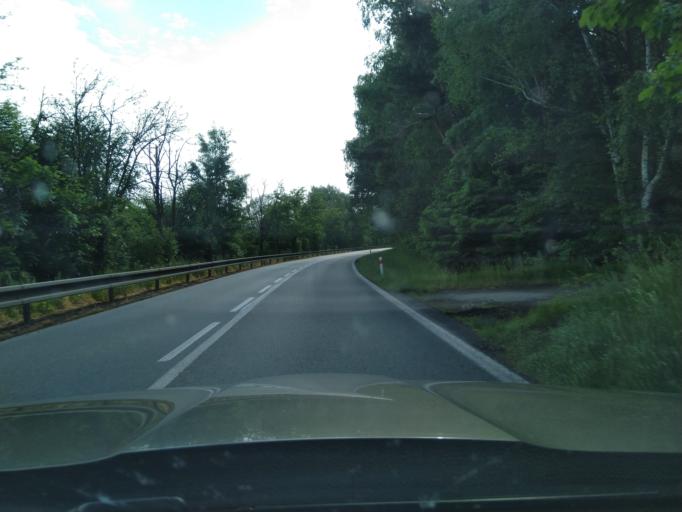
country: CZ
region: Jihocesky
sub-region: Okres Prachatice
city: Strunkovice nad Blanici
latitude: 49.0547
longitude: 14.1095
